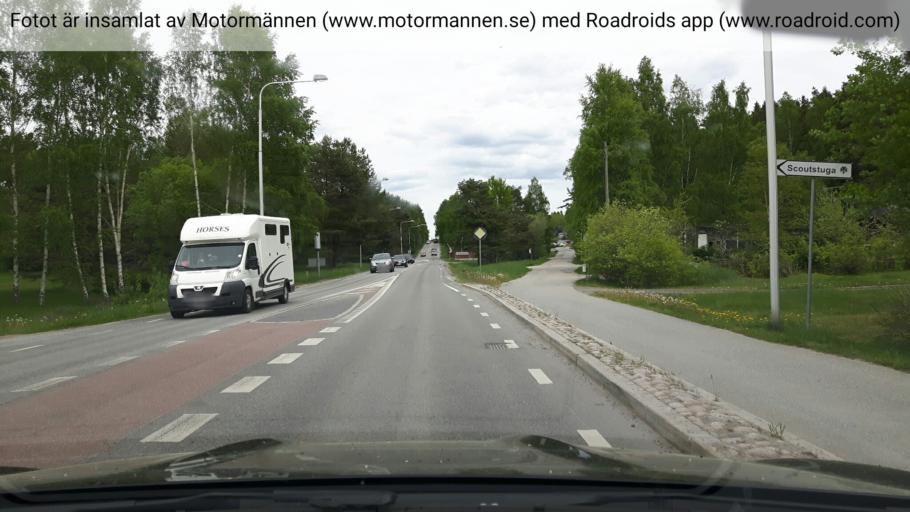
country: SE
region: Stockholm
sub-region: Osterakers Kommun
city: Akersberga
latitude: 59.4864
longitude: 18.3191
